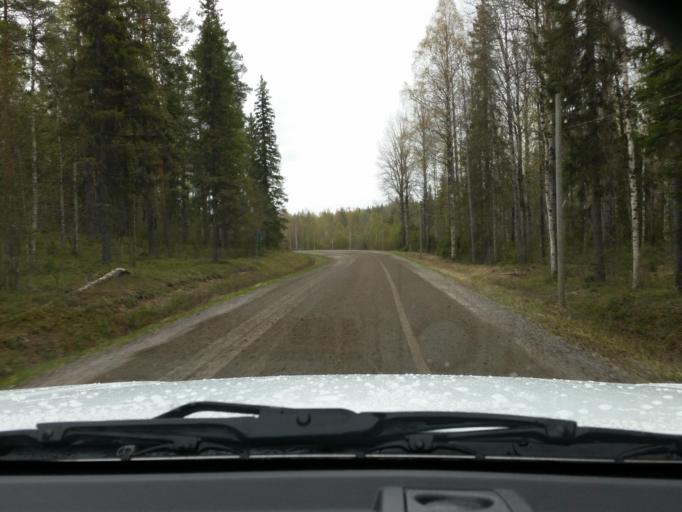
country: SE
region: Norrbotten
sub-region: Pitea Kommun
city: Norrfjarden
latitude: 65.5812
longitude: 21.4756
